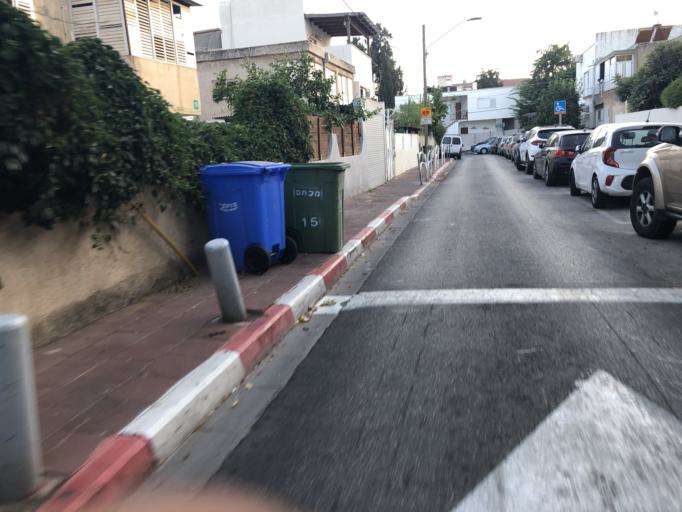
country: IL
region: Tel Aviv
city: Giv`atayim
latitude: 32.0688
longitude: 34.8178
